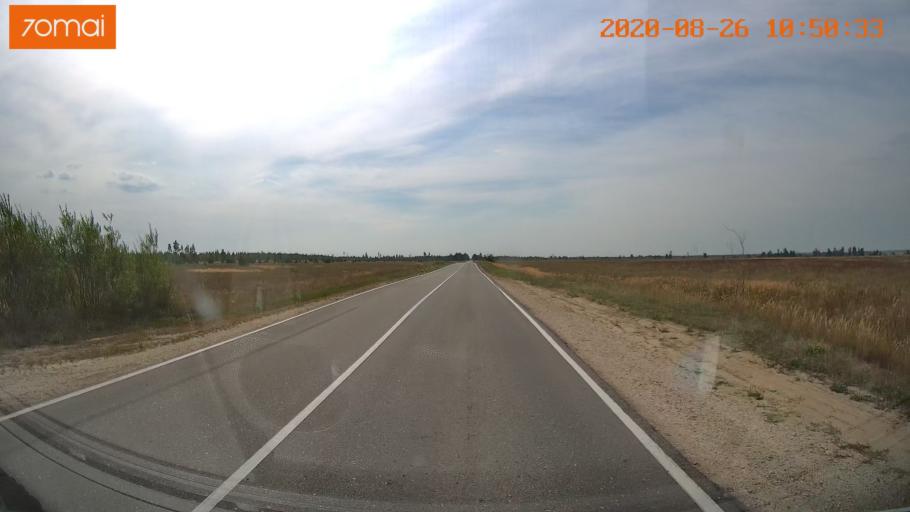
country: RU
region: Rjazan
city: Lashma
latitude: 54.6858
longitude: 41.1561
